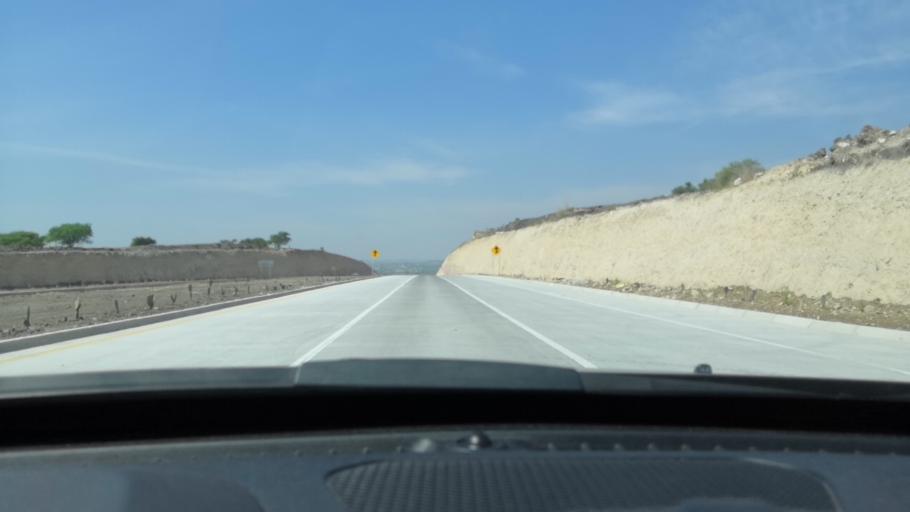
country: MX
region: Guanajuato
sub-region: Purisima del Rincon
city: Potrerillos (Guanajal)
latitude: 21.0859
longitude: -101.8260
